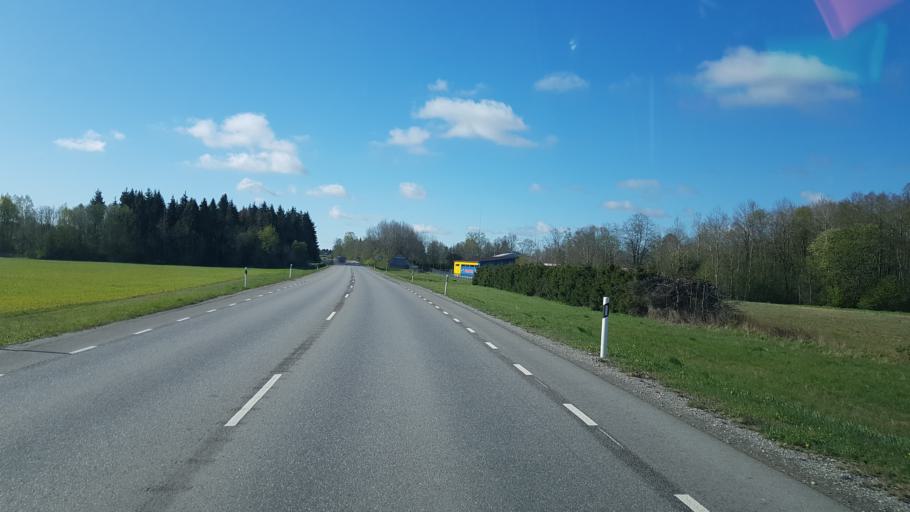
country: EE
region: Harju
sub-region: Saku vald
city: Saku
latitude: 59.2956
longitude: 24.7365
